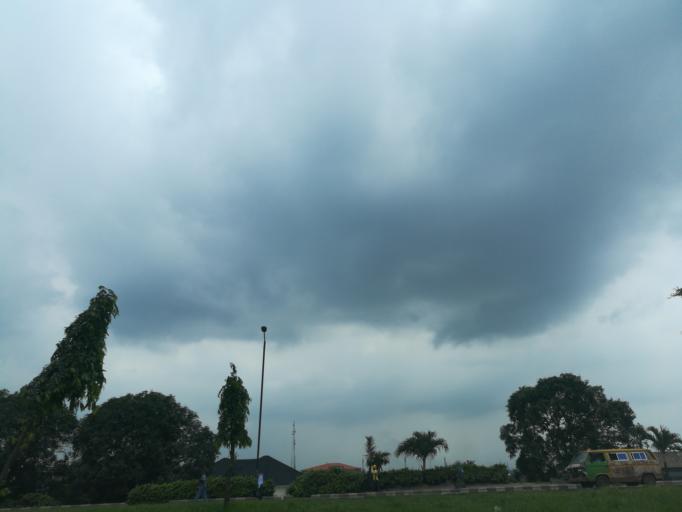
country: NG
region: Lagos
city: Ojota
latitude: 6.5972
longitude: 3.3800
